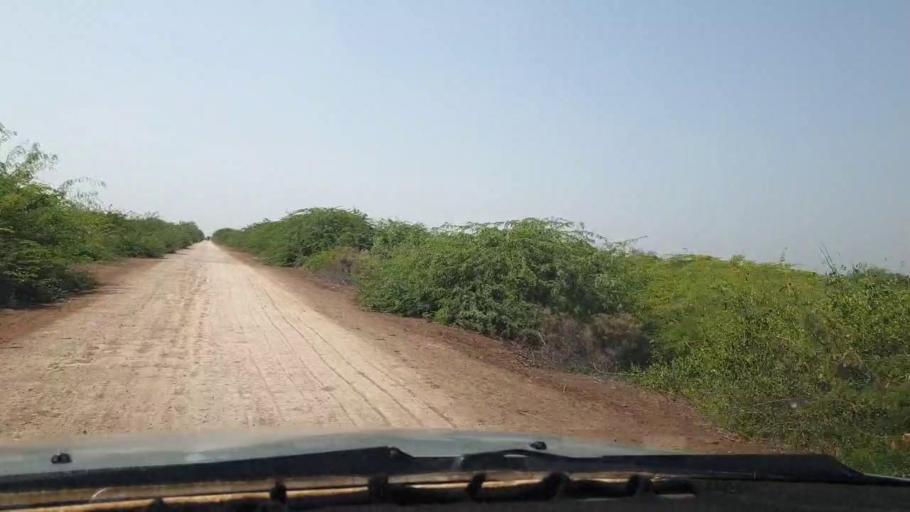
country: PK
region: Sindh
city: Tando Ghulam Ali
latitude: 25.1429
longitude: 68.8187
